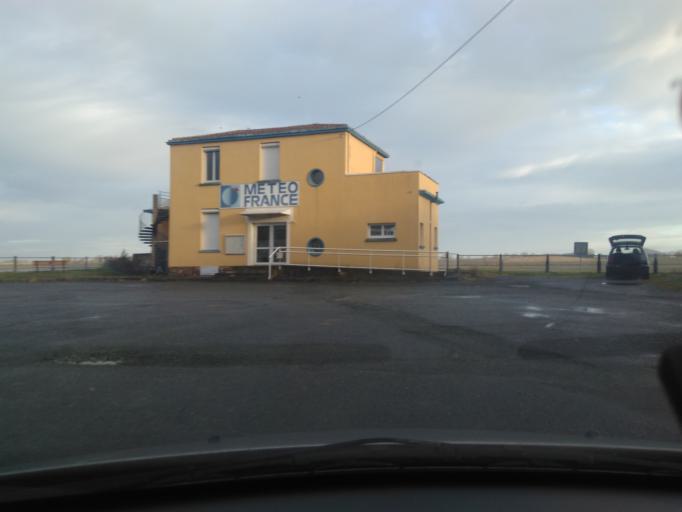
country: FR
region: Pays de la Loire
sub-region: Departement de la Vendee
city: Dompierre-sur-Yon
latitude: 46.6993
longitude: -1.3792
